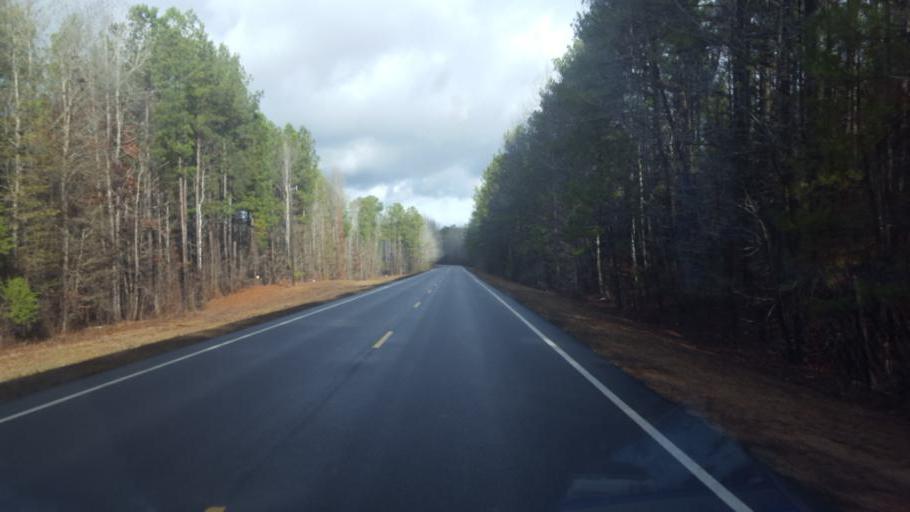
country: US
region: Georgia
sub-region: Butts County
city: Indian Springs
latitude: 33.1886
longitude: -83.8478
